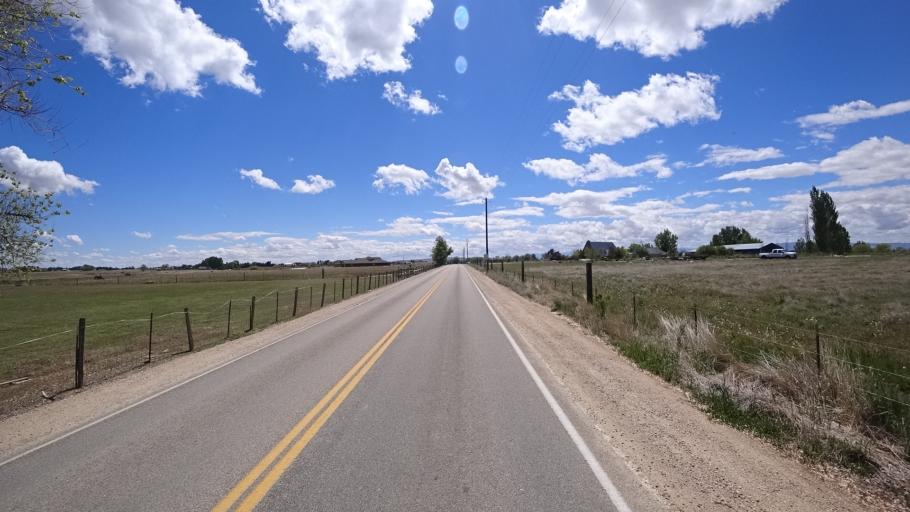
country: US
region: Idaho
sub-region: Ada County
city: Kuna
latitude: 43.5605
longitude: -116.4536
